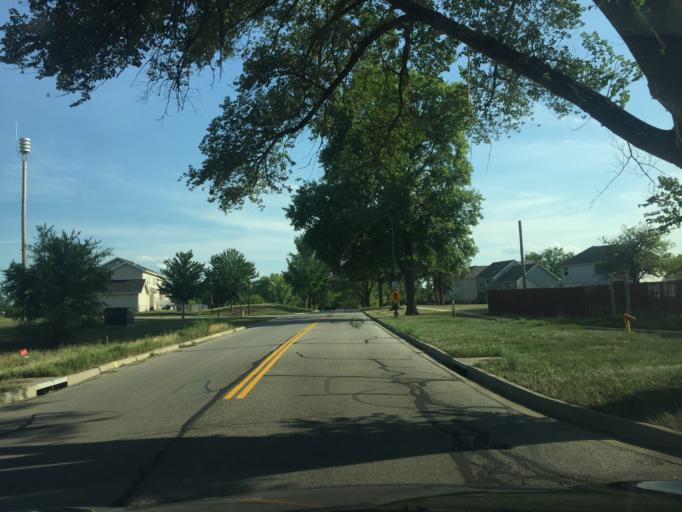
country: US
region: Kansas
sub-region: Leavenworth County
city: Leavenworth
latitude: 39.3449
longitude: -94.9311
